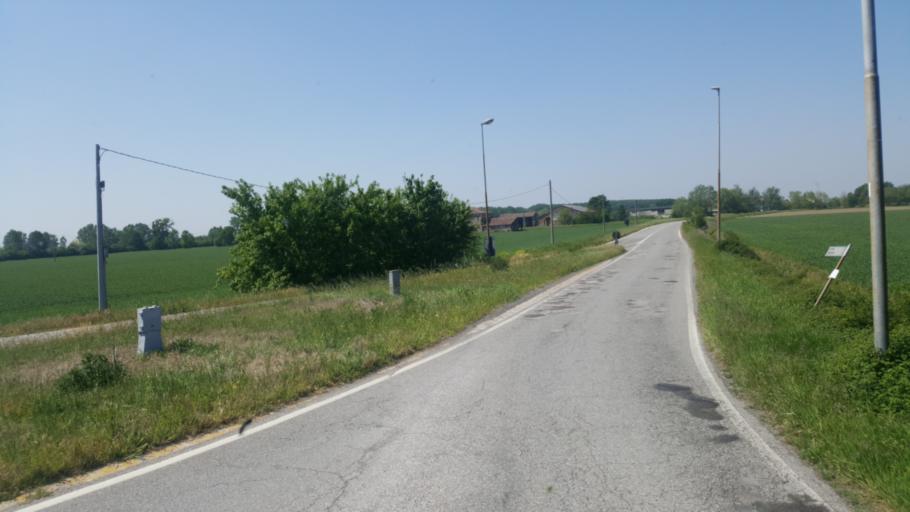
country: IT
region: Lombardy
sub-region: Provincia di Mantova
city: Schivenoglia
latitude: 45.0203
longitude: 11.0728
